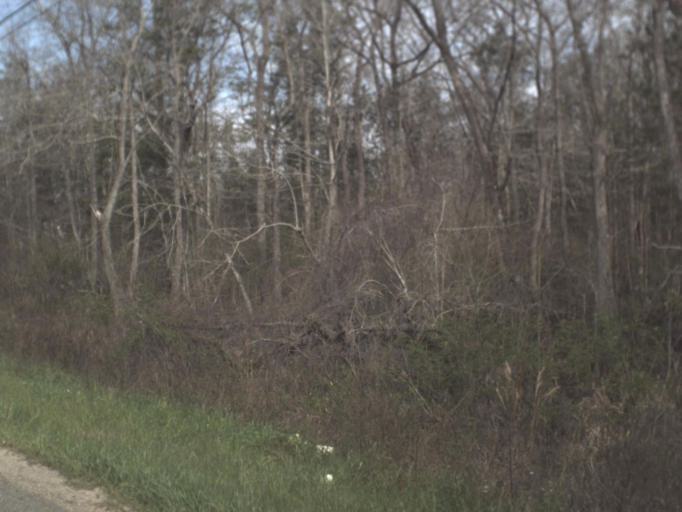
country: US
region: Florida
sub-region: Leon County
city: Tallahassee
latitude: 30.4476
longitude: -84.3560
